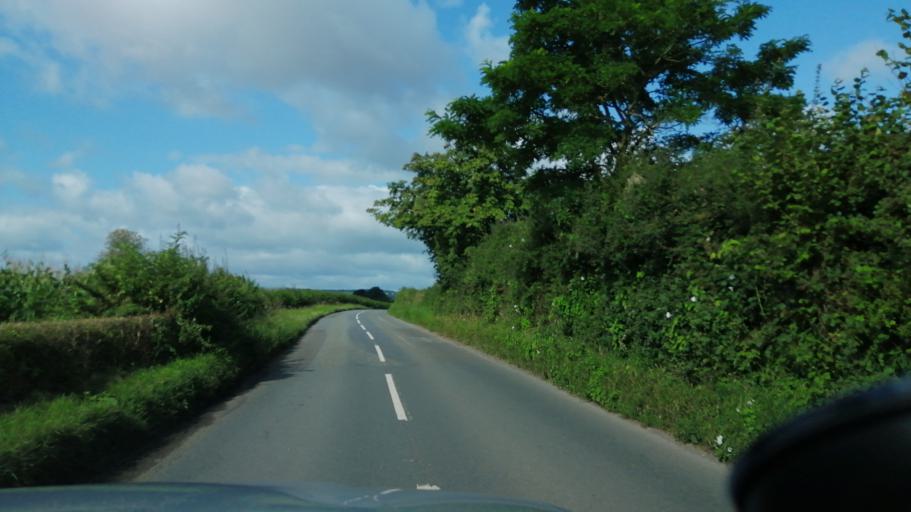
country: GB
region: England
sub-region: Herefordshire
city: Madley
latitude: 52.0403
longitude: -2.8306
